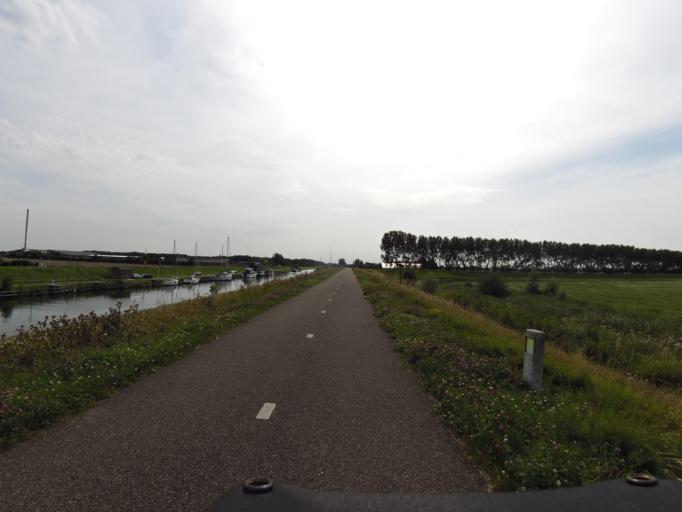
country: NL
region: South Holland
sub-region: Gemeente Goeree-Overflakkee
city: Middelharnis
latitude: 51.7724
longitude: 4.1869
